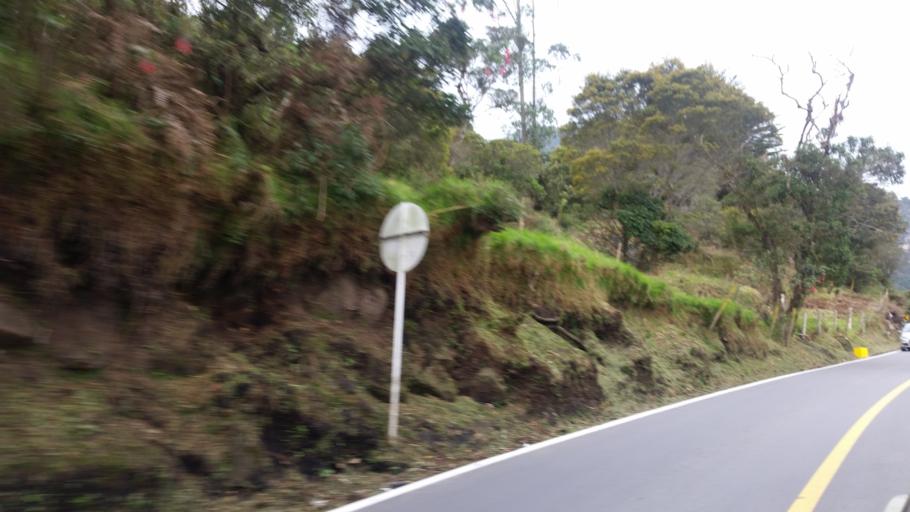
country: CO
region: Cundinamarca
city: Choachi
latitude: 4.5577
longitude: -73.9514
